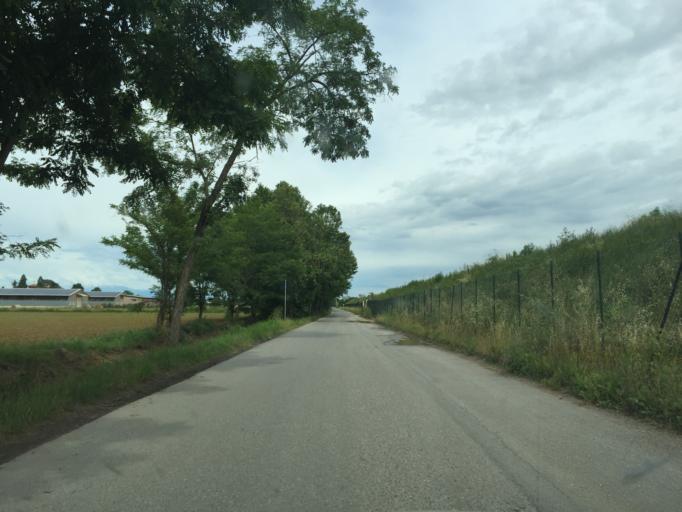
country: IT
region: Lombardy
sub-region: Provincia di Brescia
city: Montirone
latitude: 45.4500
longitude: 10.2646
